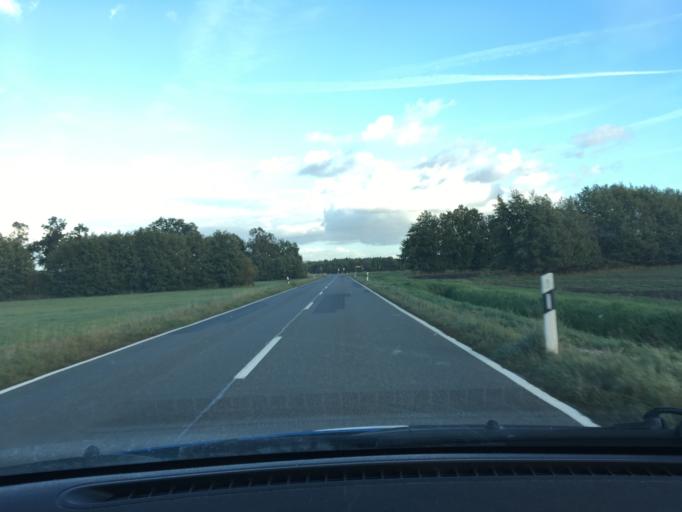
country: DE
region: Lower Saxony
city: Hittbergen
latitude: 53.3180
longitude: 10.6114
